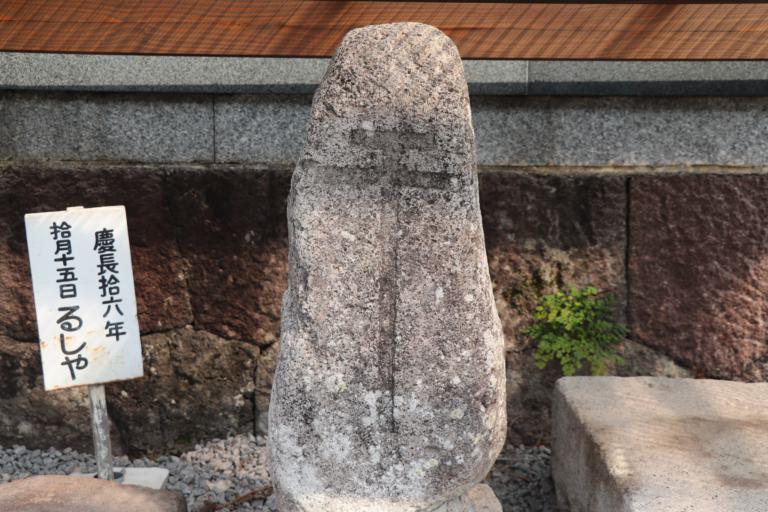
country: JP
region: Nagasaki
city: Shimabara
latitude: 32.7191
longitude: 130.3483
